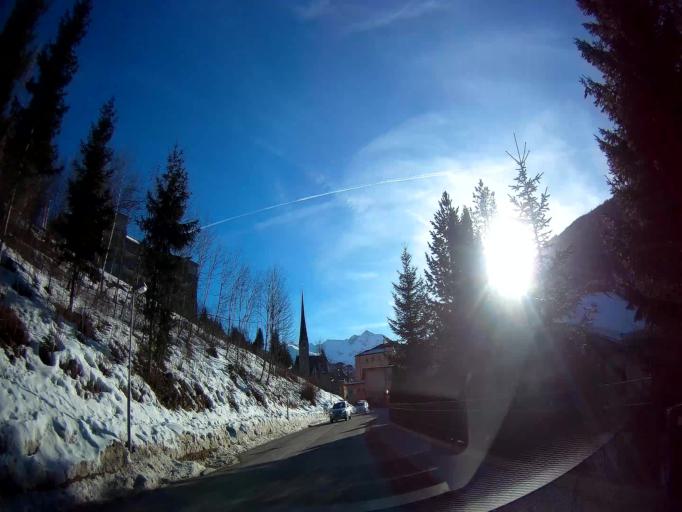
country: AT
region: Salzburg
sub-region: Politischer Bezirk Sankt Johann im Pongau
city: Bad Gastein
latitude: 47.1210
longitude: 13.1396
